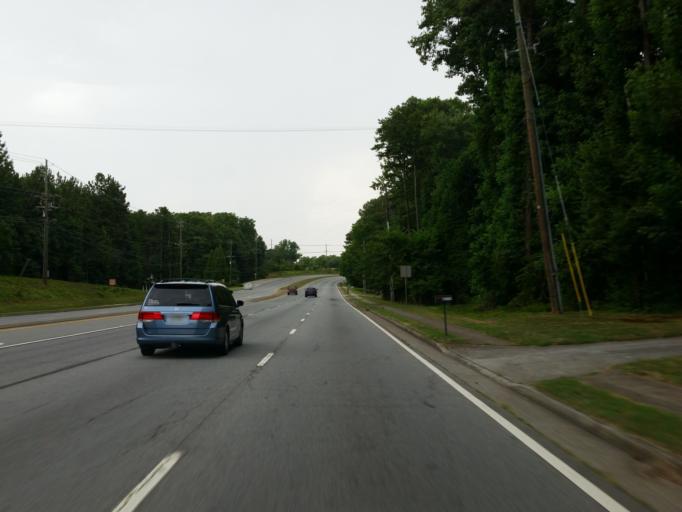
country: US
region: Georgia
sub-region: Fulton County
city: Roswell
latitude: 34.0618
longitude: -84.4089
